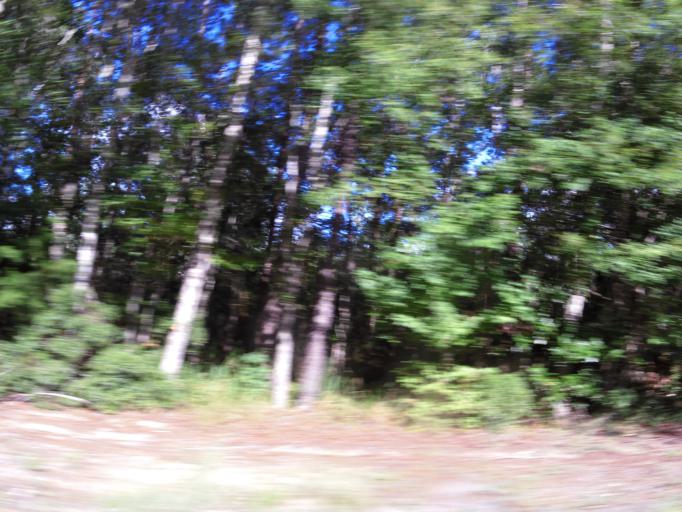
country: US
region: Georgia
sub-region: Camden County
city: Woodbine
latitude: 31.0175
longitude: -81.7312
